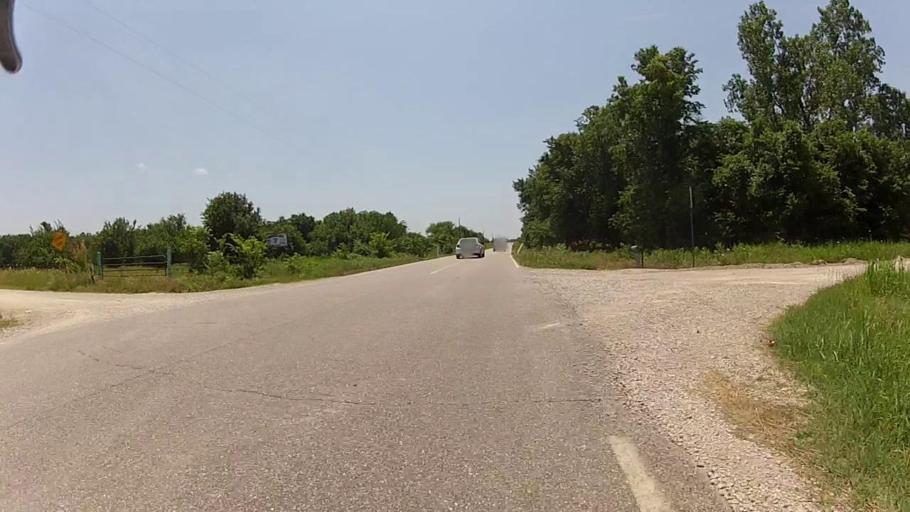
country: US
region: Kansas
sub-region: Montgomery County
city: Cherryvale
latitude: 37.2303
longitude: -95.5378
